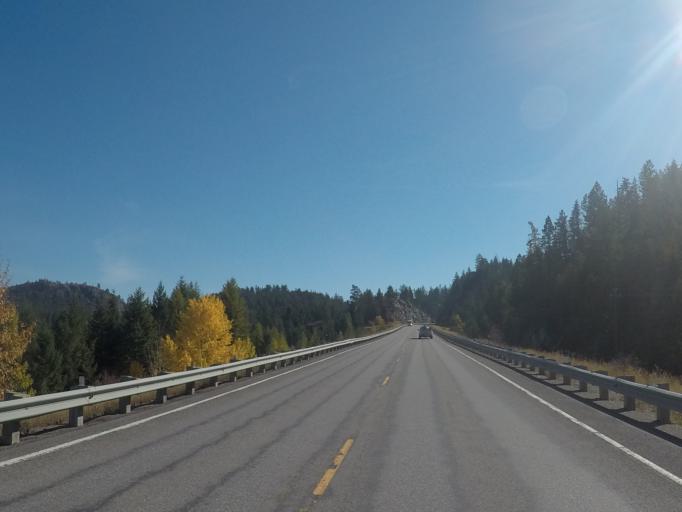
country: US
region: Montana
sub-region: Flathead County
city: Lakeside
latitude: 47.9897
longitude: -114.2040
